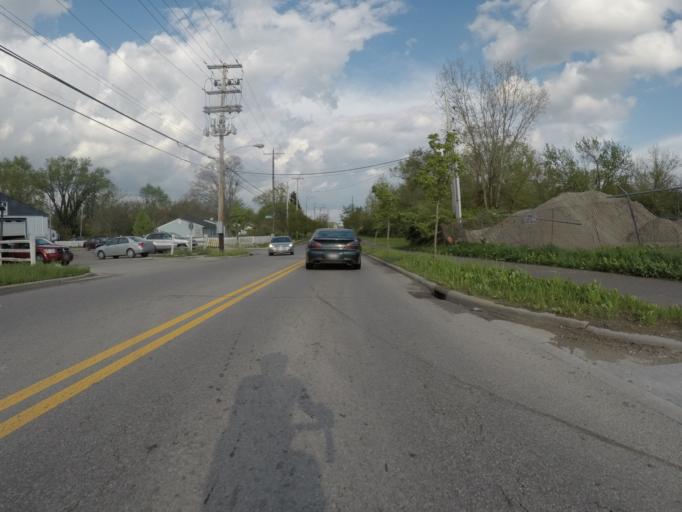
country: US
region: Ohio
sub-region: Franklin County
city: Bexley
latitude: 40.0135
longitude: -82.9644
